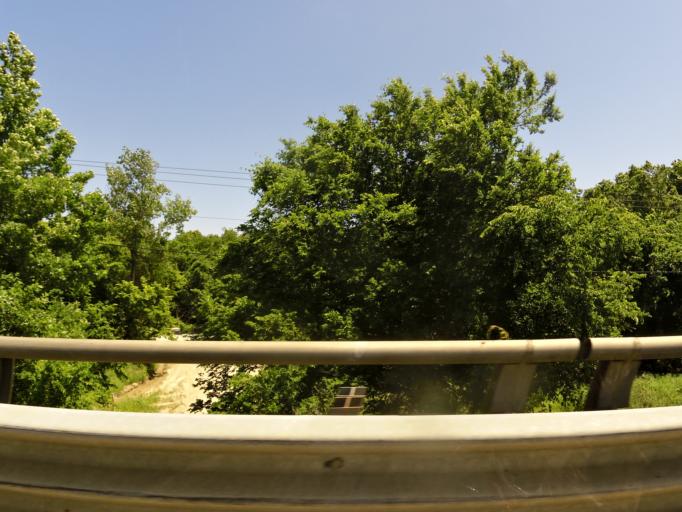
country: US
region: Georgia
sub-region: Richmond County
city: Augusta
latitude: 33.4801
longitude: -81.9524
